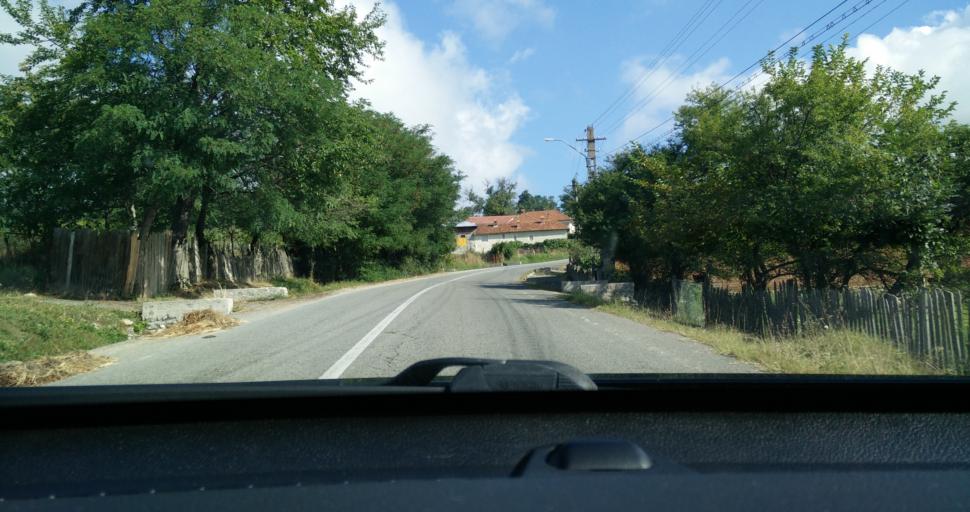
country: RO
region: Gorj
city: Novaci-Straini
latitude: 45.1837
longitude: 23.6816
